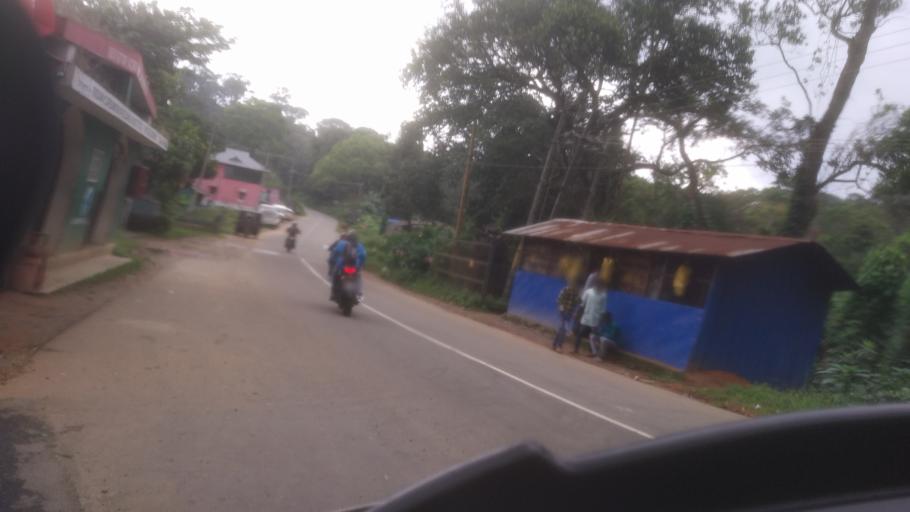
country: IN
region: Tamil Nadu
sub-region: Theni
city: Kombai
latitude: 9.8909
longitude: 77.1561
